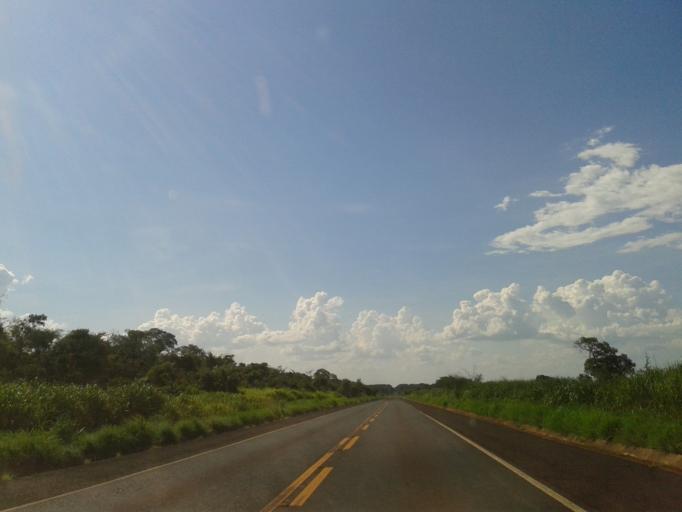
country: BR
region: Minas Gerais
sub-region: Santa Vitoria
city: Santa Vitoria
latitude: -19.0475
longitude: -50.4046
